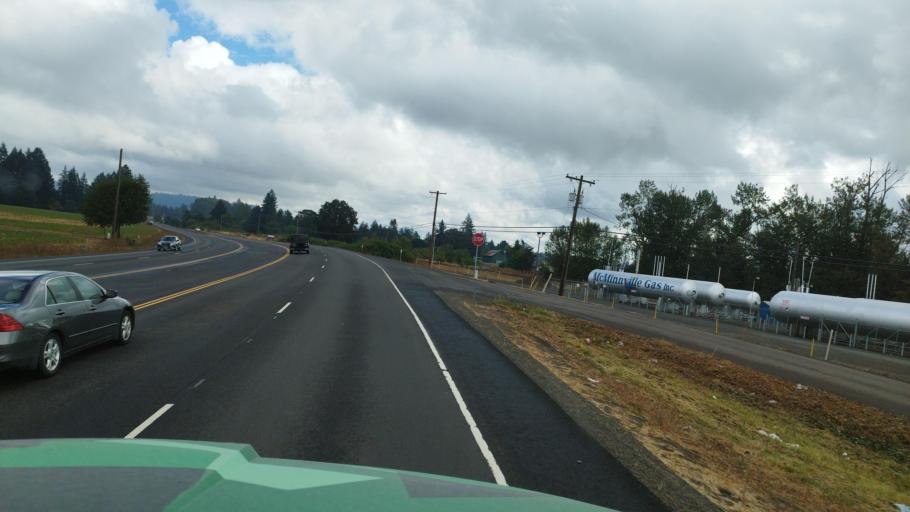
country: US
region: Oregon
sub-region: Yamhill County
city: Lafayette
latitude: 45.2399
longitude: -123.1417
